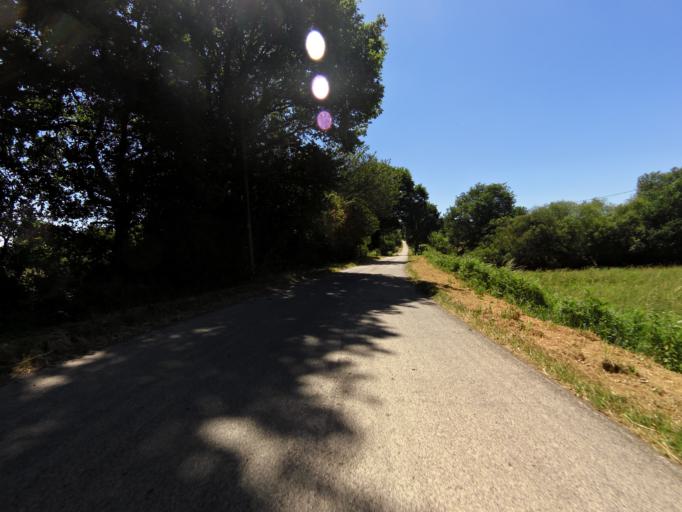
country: FR
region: Brittany
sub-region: Departement du Morbihan
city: Molac
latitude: 47.7191
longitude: -2.4140
